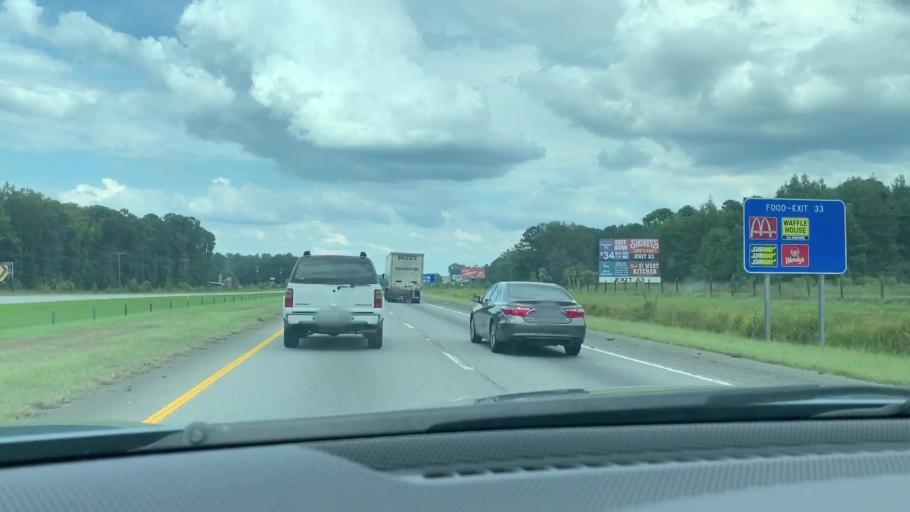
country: US
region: South Carolina
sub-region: Hampton County
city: Yemassee
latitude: 32.6193
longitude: -80.8903
